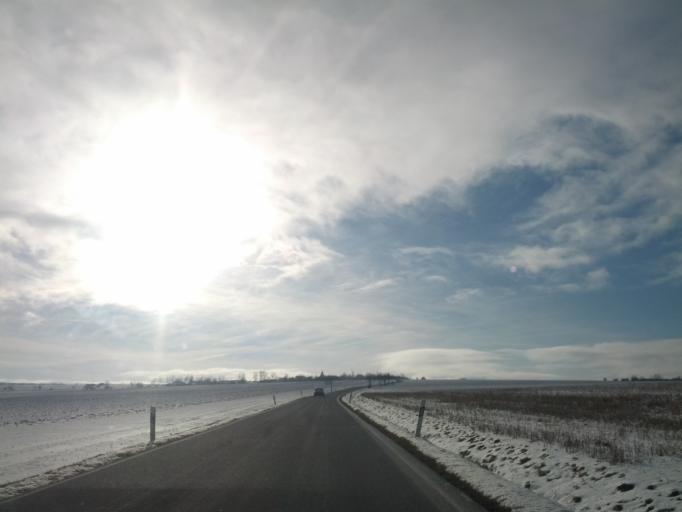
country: DE
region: Thuringia
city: Weberstedt
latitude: 51.0726
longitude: 10.5064
